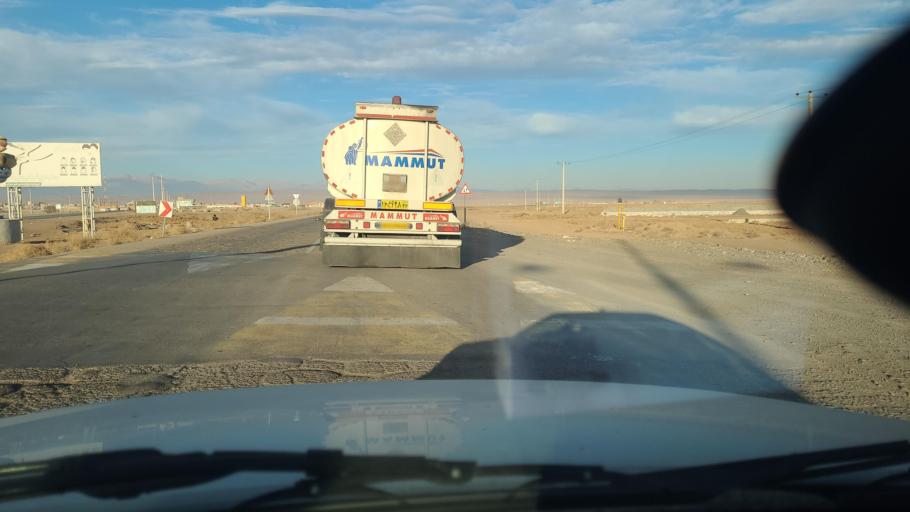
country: IR
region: Razavi Khorasan
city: Neqab
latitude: 36.6120
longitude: 57.5946
